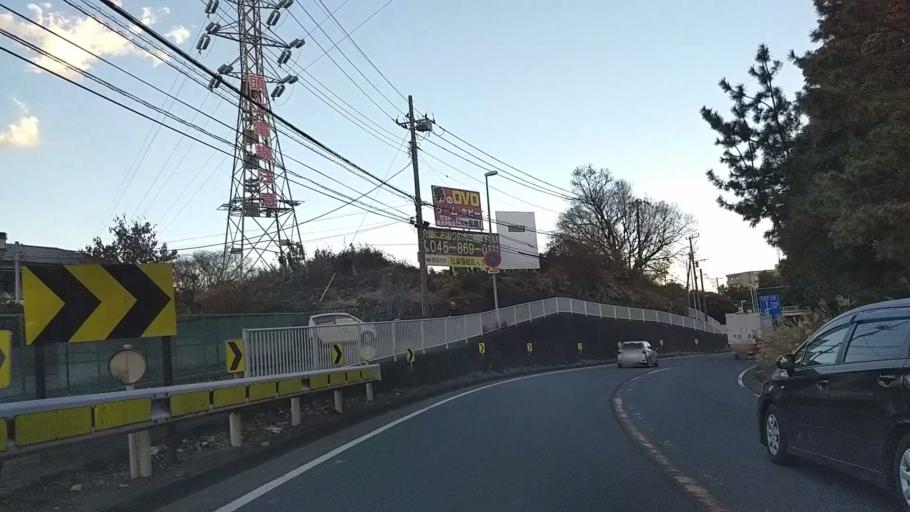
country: JP
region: Kanagawa
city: Fujisawa
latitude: 35.3844
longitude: 139.5149
